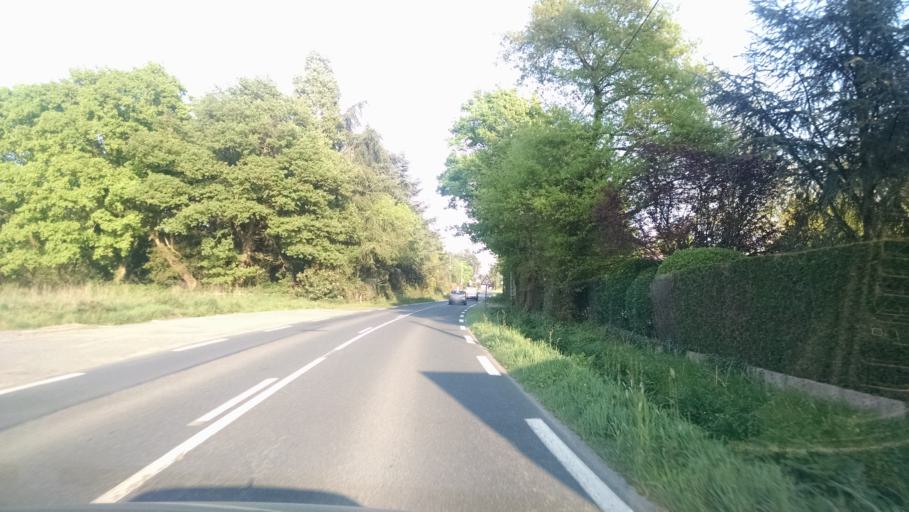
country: FR
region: Pays de la Loire
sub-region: Departement de la Loire-Atlantique
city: Gorges
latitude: 47.0918
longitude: -1.3004
